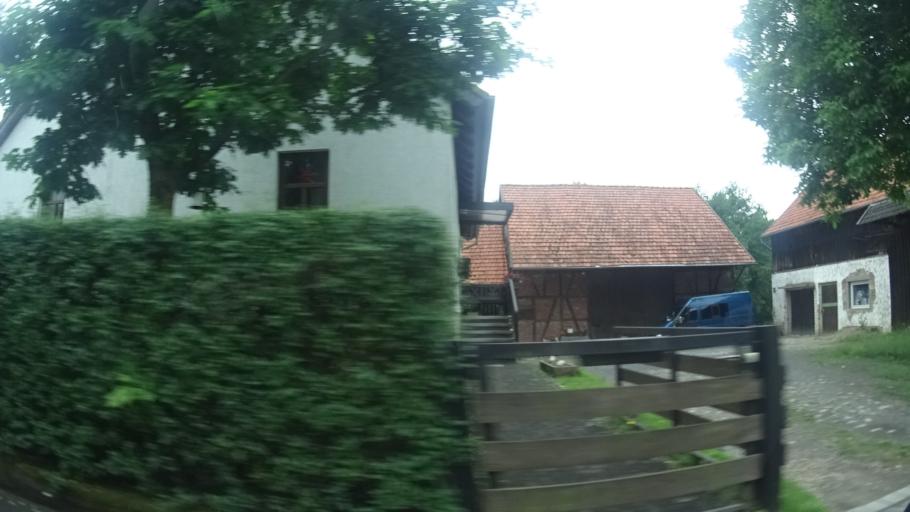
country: DE
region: Hesse
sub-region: Regierungsbezirk Darmstadt
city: Bad Soden-Salmunster
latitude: 50.2719
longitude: 9.3782
